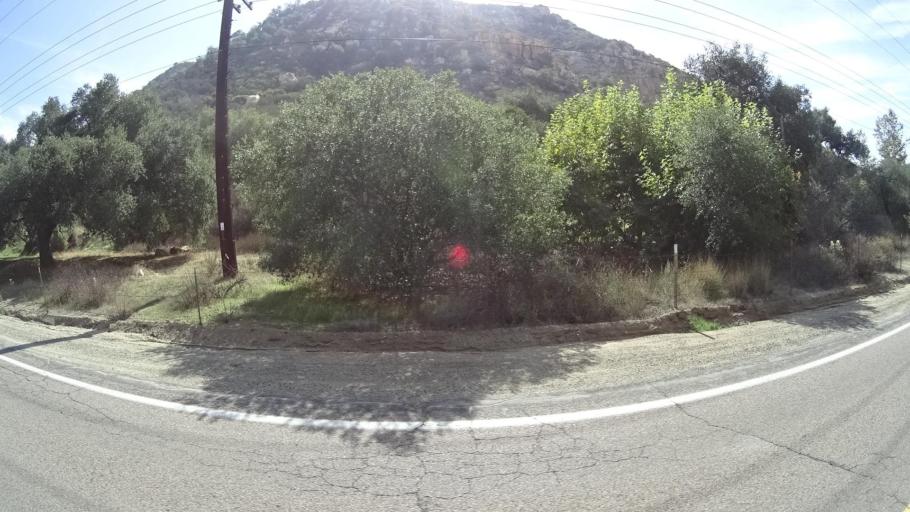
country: US
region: California
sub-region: San Diego County
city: Harbison Canyon
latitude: 32.8275
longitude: -116.8222
